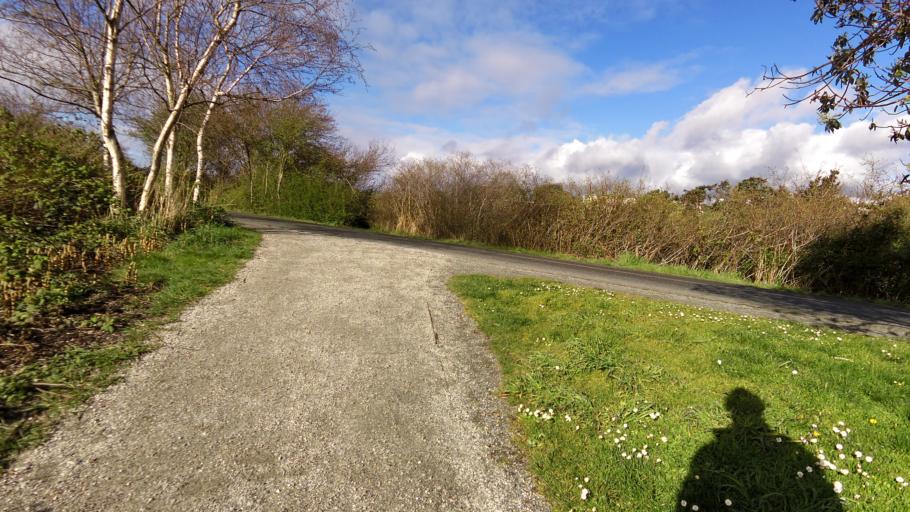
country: CA
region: British Columbia
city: Victoria
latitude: 48.4413
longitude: -123.3806
